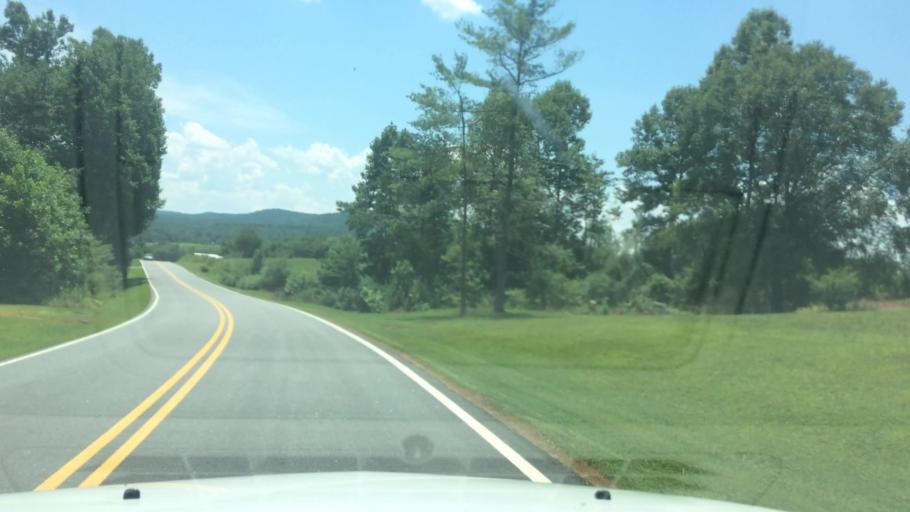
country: US
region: North Carolina
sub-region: Alexander County
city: Taylorsville
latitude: 35.9397
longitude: -81.2687
